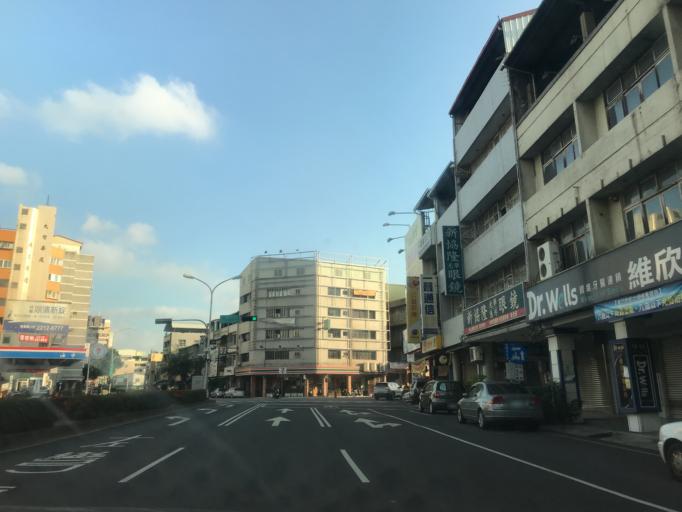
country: TW
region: Taiwan
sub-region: Taichung City
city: Taichung
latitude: 24.1310
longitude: 120.6904
